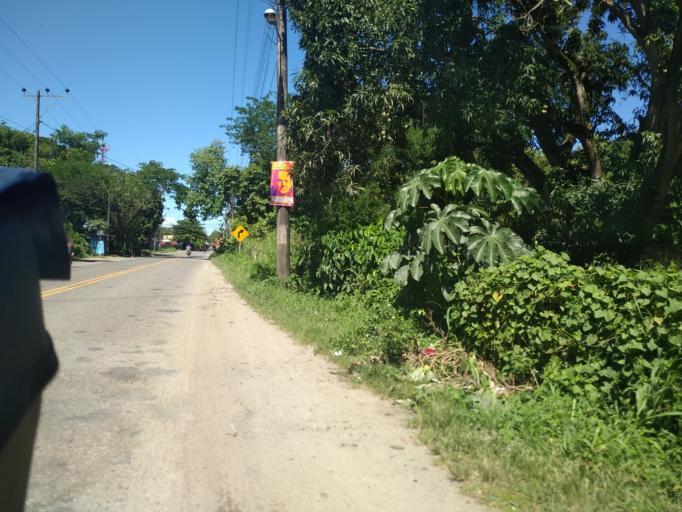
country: CO
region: Cundinamarca
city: Puerto Salgar
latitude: 5.4753
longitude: -74.6466
